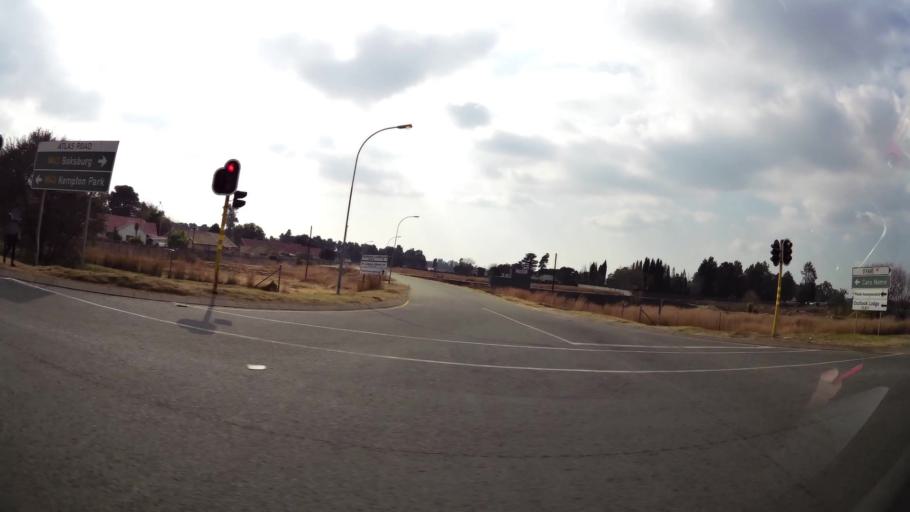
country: ZA
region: Gauteng
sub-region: Ekurhuleni Metropolitan Municipality
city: Benoni
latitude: -26.1269
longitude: 28.2631
